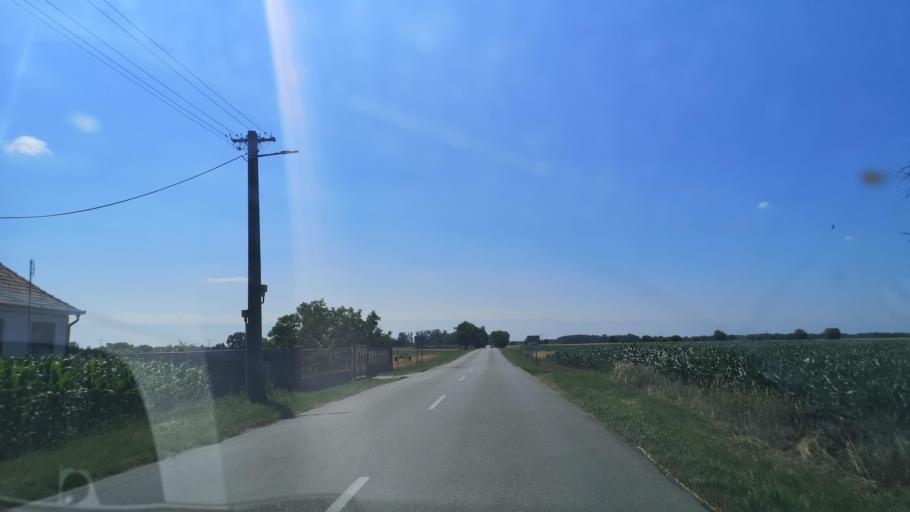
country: SK
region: Bratislavsky
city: Senec
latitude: 48.0982
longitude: 17.4803
